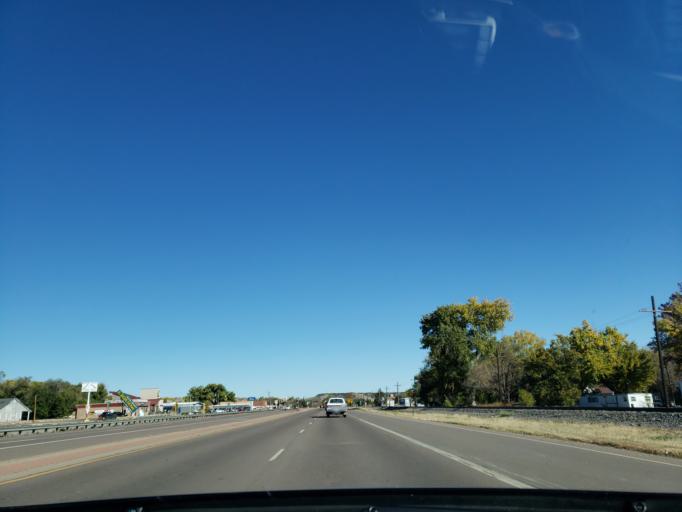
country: US
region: Colorado
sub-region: Fremont County
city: Lincoln Park
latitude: 38.4479
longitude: -105.2139
